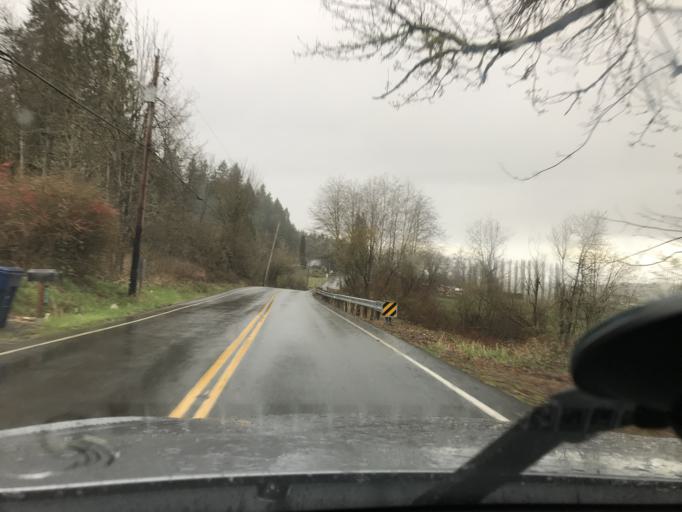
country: US
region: Washington
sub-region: King County
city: Ames Lake
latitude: 47.6710
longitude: -121.9768
